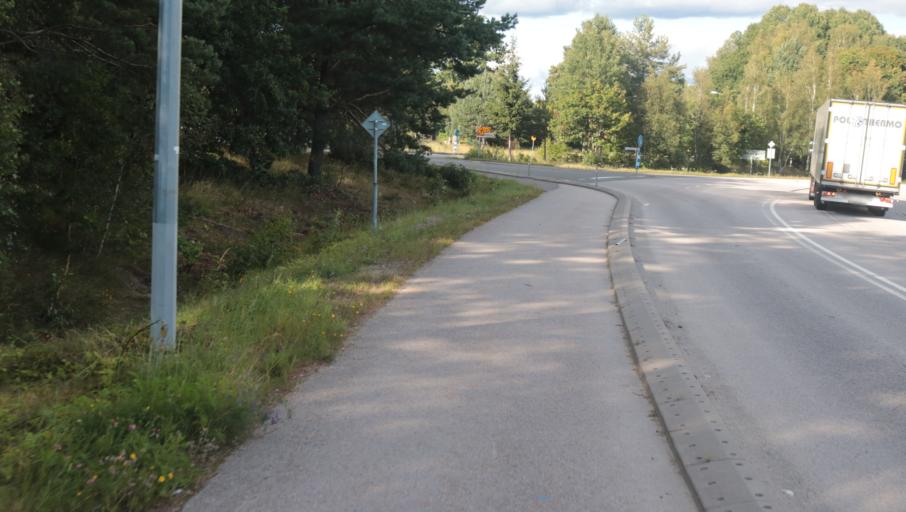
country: SE
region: Blekinge
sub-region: Karlshamns Kommun
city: Karlshamn
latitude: 56.1892
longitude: 14.9275
